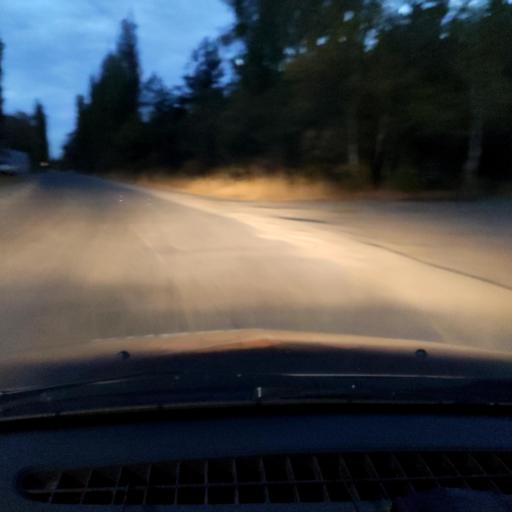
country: RU
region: Voronezj
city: Pridonskoy
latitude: 51.6744
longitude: 39.1024
